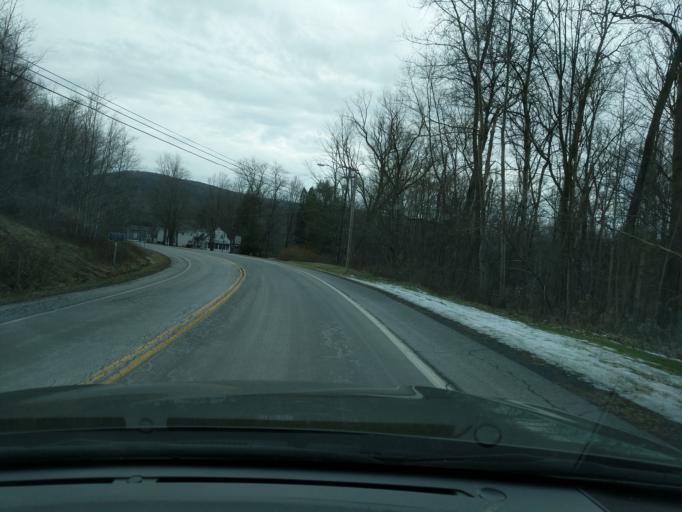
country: US
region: New York
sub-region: Tompkins County
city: East Ithaca
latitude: 42.3838
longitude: -76.4023
